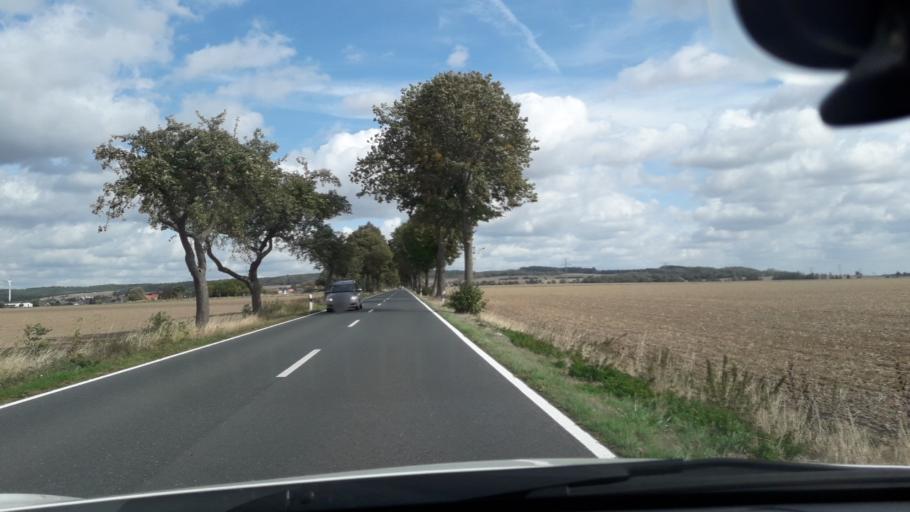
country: DE
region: Lower Saxony
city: Alt Wallmoden
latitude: 52.0439
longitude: 10.3135
